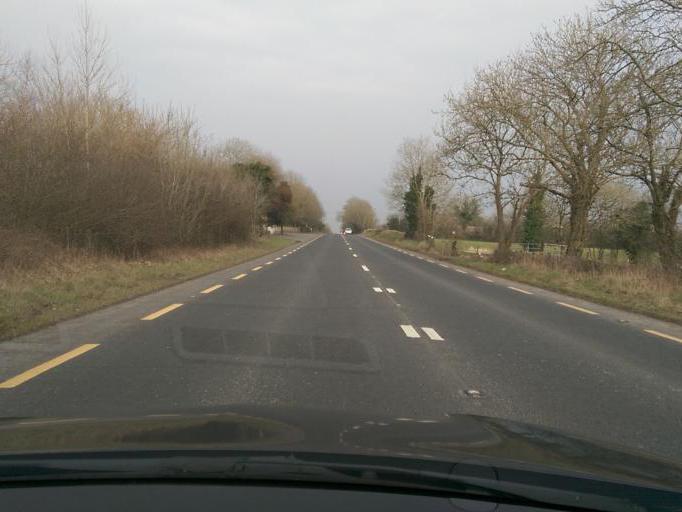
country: IE
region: Connaught
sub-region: Roscommon
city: Roscommon
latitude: 53.6409
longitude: -8.1556
